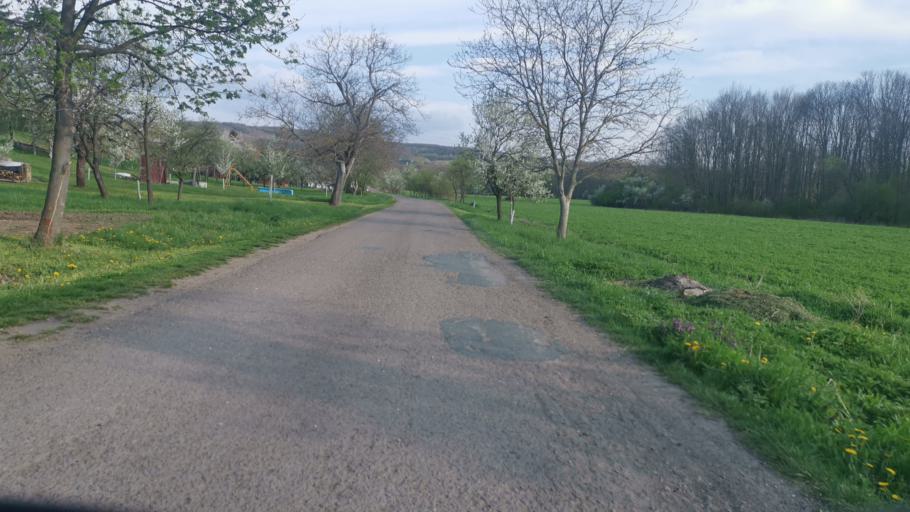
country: CZ
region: South Moravian
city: Petrov
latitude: 48.8489
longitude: 17.3010
